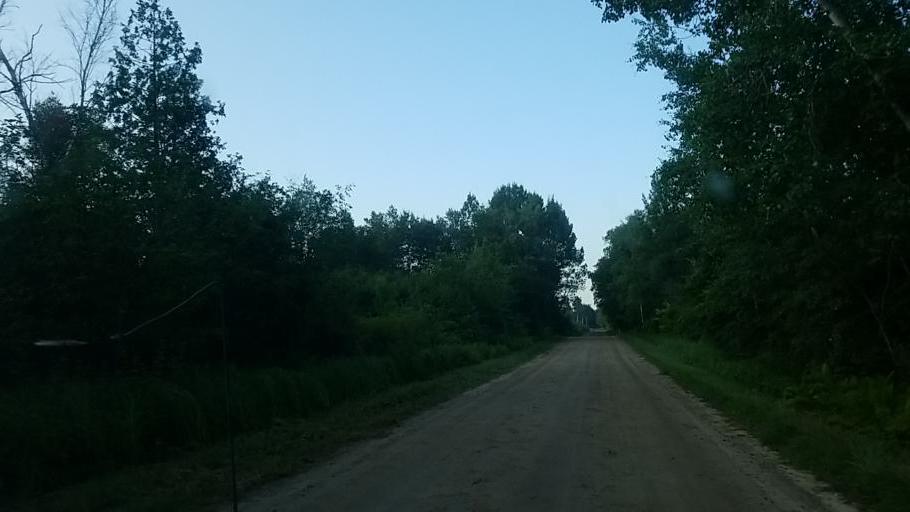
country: US
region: Michigan
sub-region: Osceola County
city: Evart
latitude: 43.9063
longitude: -85.1678
